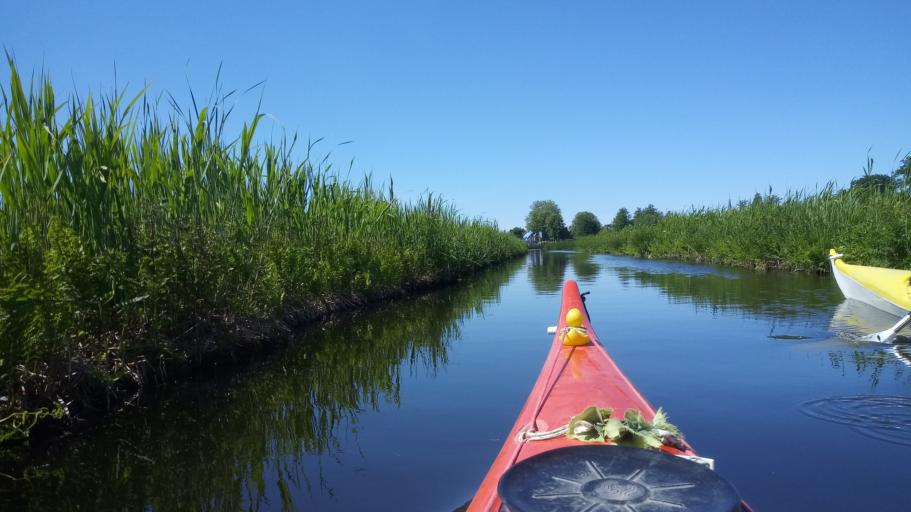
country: NL
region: South Holland
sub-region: Gemeente Nieuwkoop
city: Nieuwkoop
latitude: 52.1462
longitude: 4.7817
